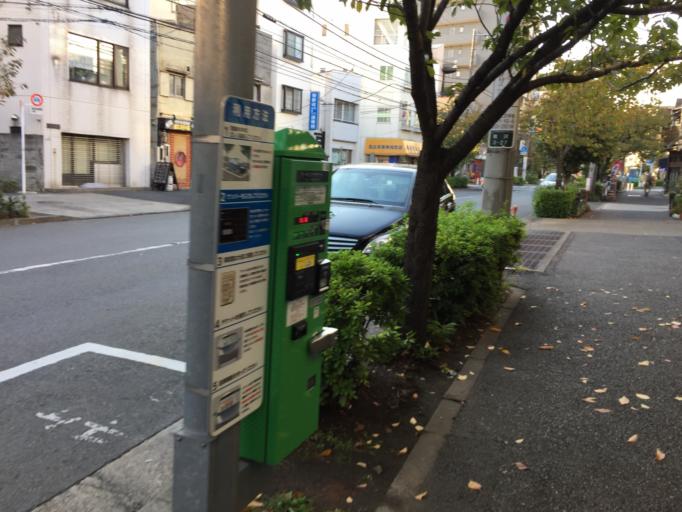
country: JP
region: Tokyo
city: Tokyo
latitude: 35.6309
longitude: 139.6513
